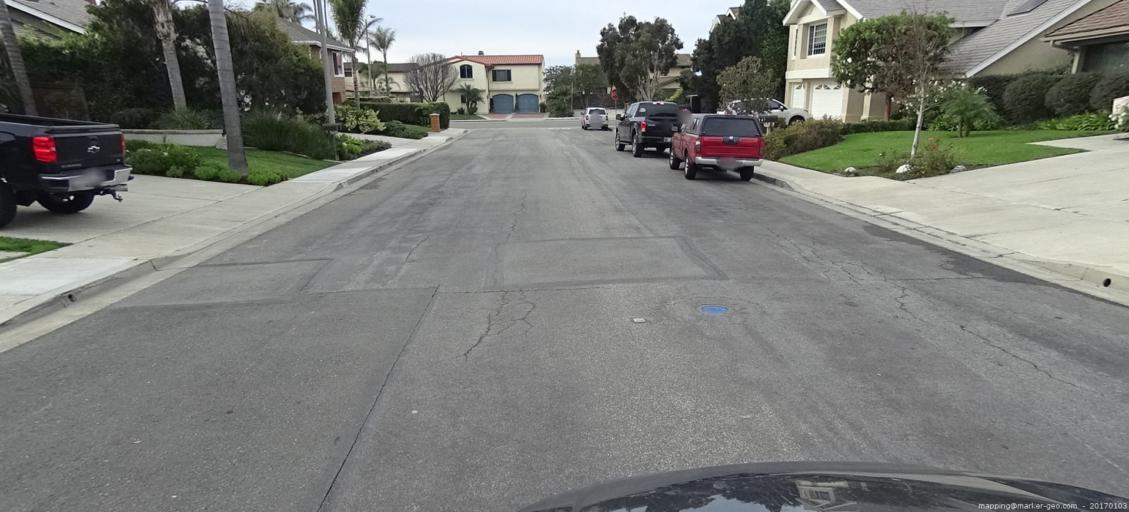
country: US
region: California
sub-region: Orange County
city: San Clemente
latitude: 33.4478
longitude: -117.6509
